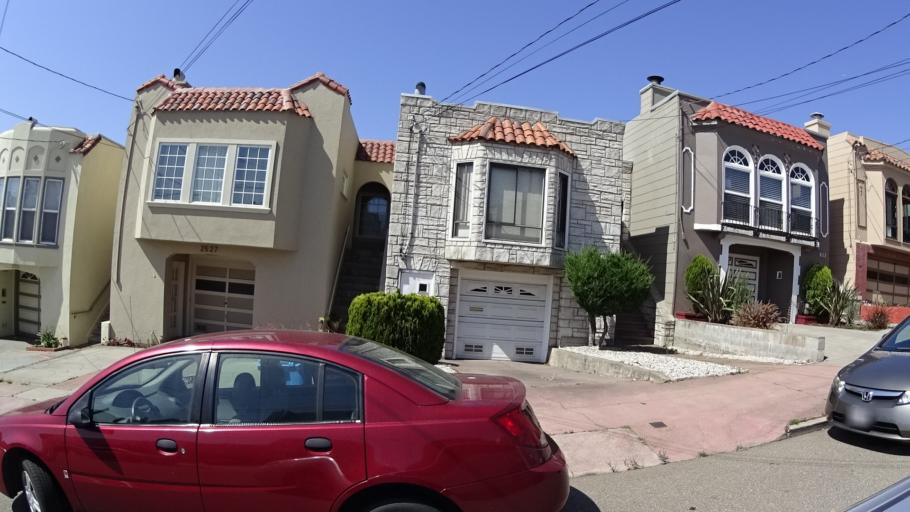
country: US
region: California
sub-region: San Mateo County
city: Daly City
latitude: 37.7403
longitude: -122.4863
